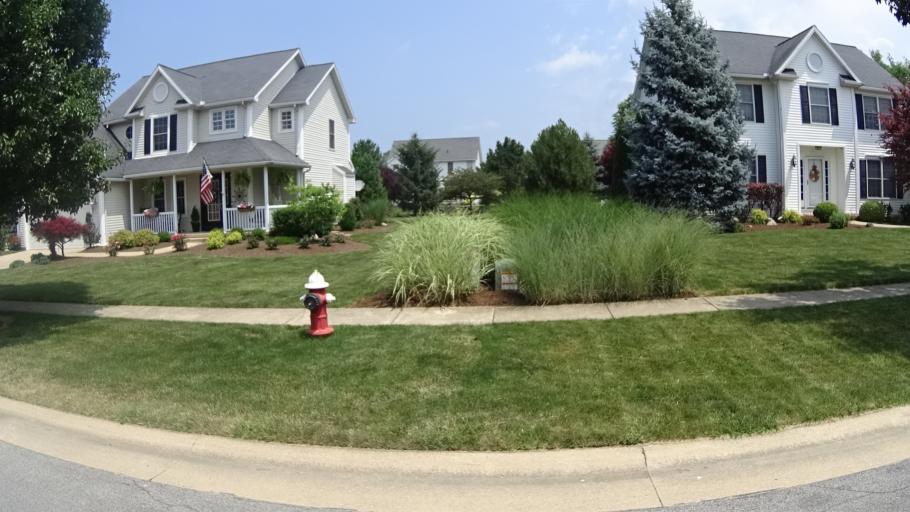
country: US
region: Ohio
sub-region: Erie County
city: Huron
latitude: 41.3845
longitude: -82.5323
